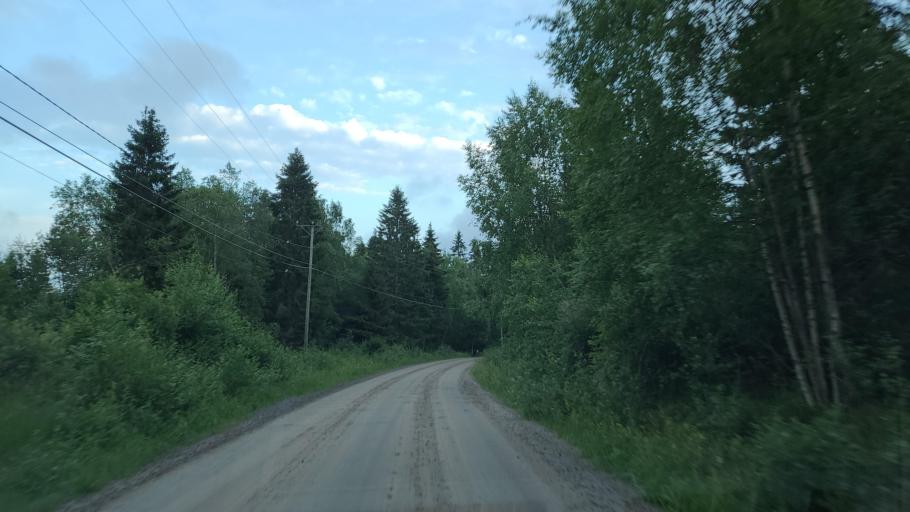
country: FI
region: Ostrobothnia
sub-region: Vaasa
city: Replot
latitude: 63.3042
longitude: 21.1539
